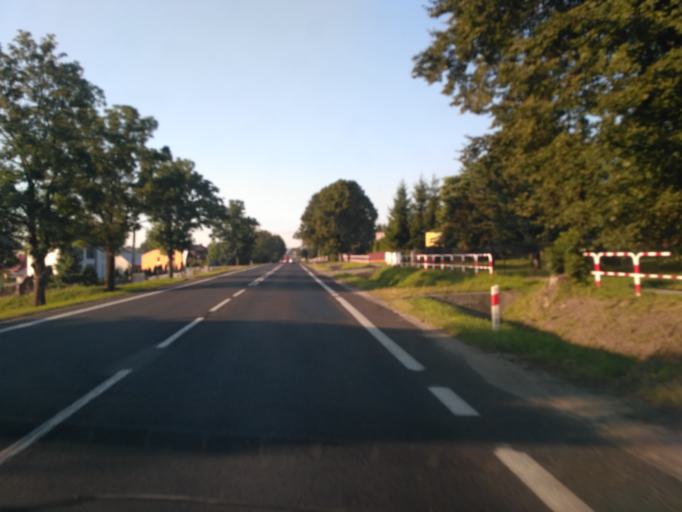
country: PL
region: Subcarpathian Voivodeship
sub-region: Powiat krosnienski
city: Miejsce Piastowe
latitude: 49.6422
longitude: 21.7847
